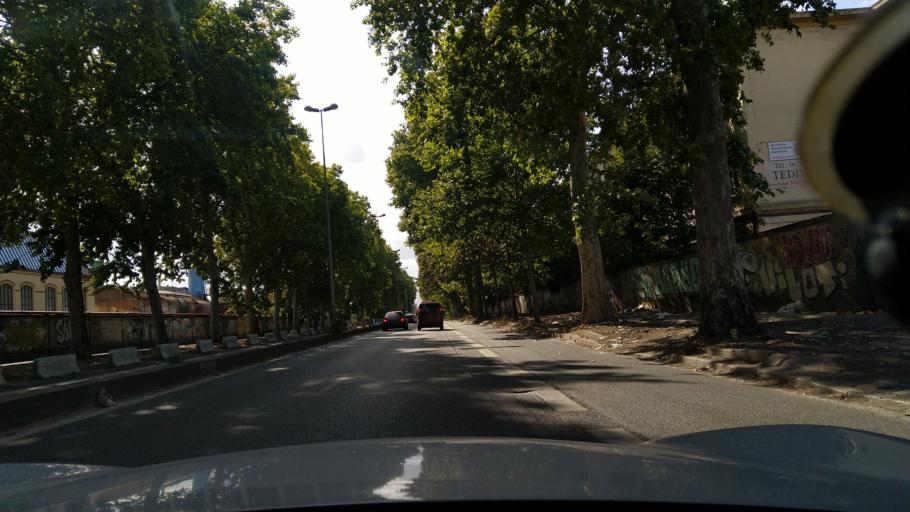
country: FR
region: Ile-de-France
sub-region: Departement de Seine-Saint-Denis
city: Bobigny
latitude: 48.9003
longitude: 2.4512
